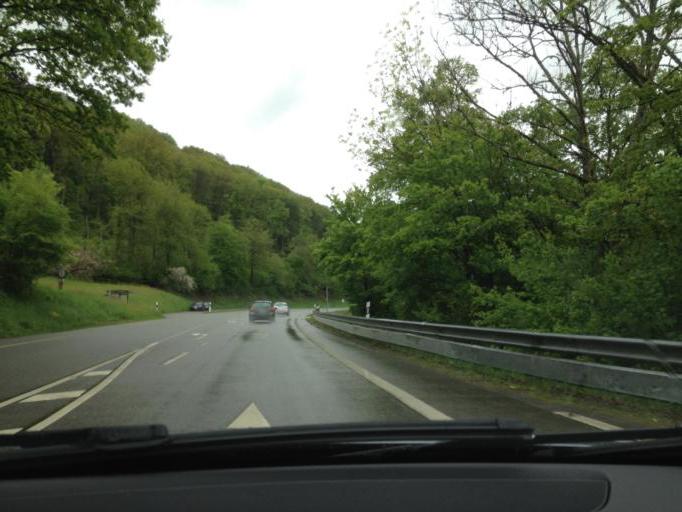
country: DE
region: Baden-Wuerttemberg
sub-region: Karlsruhe Region
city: Zwingenberg
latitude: 49.4328
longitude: 9.0067
